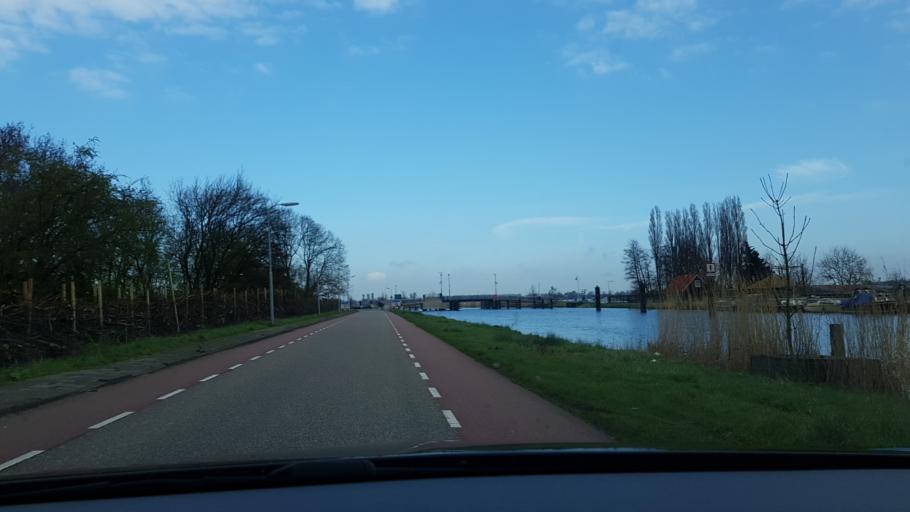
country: NL
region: North Holland
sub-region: Gemeente Haarlemmermeer
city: Hoofddorp
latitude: 52.3700
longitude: 4.7578
